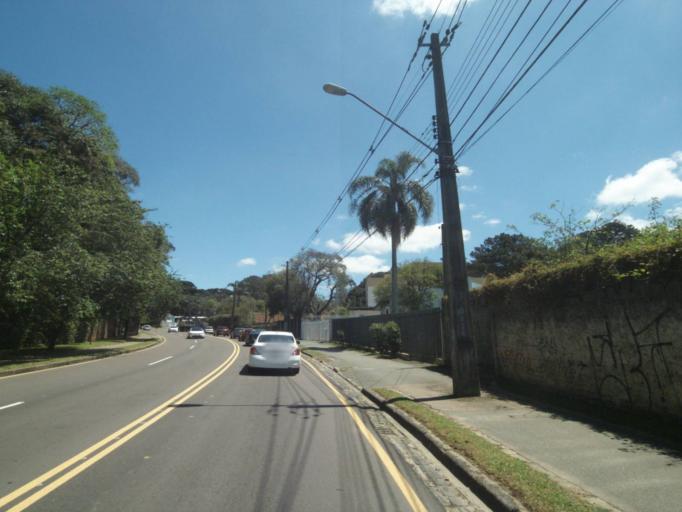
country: BR
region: Parana
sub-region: Curitiba
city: Curitiba
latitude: -25.3872
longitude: -49.2688
